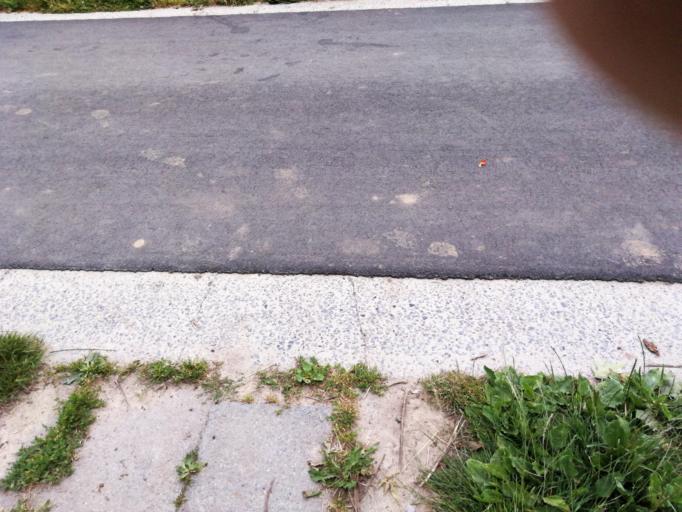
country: BE
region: Flanders
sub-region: Provincie West-Vlaanderen
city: Wielsbeke
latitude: 50.8903
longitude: 3.3429
